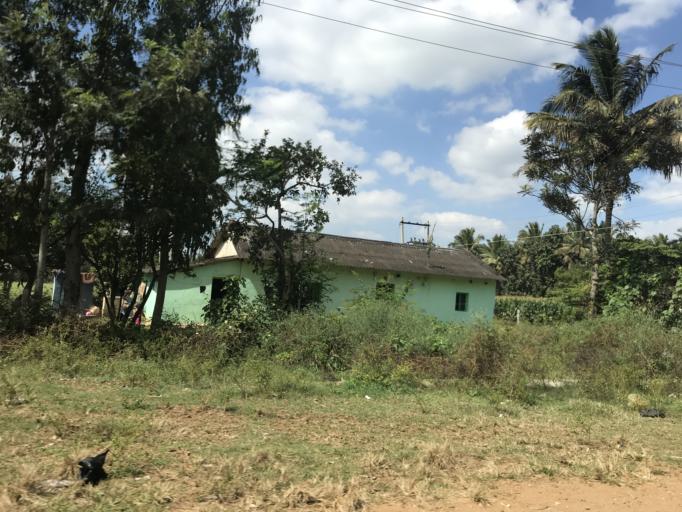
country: IN
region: Karnataka
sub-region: Mysore
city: Hunsur
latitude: 12.2584
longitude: 76.2699
